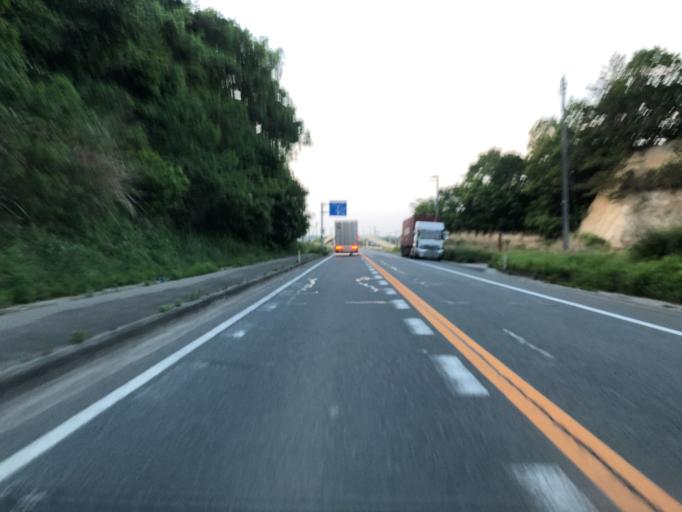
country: JP
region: Fukushima
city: Namie
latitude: 37.5488
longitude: 141.0062
